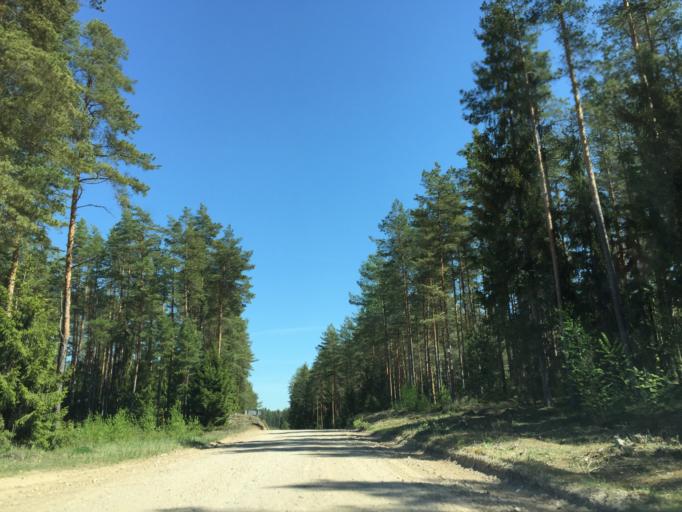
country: LV
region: Ikskile
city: Ikskile
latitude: 56.7336
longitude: 24.5259
